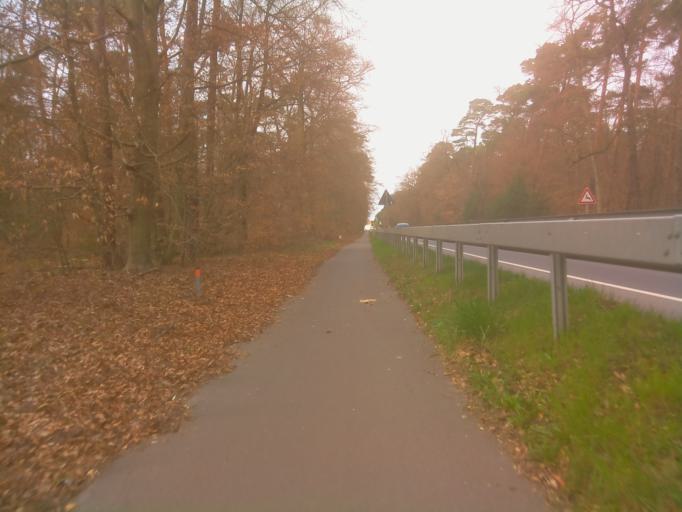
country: DE
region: Hesse
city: Lampertheim
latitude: 49.5967
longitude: 8.5294
